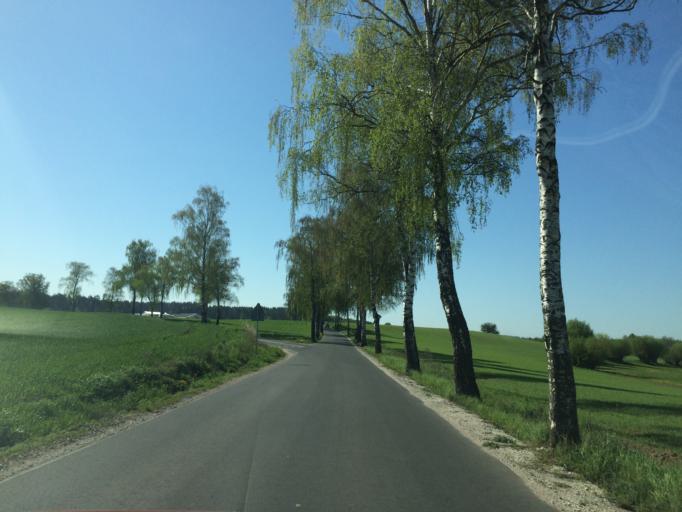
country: PL
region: Warmian-Masurian Voivodeship
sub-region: Powiat nowomiejski
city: Nowe Miasto Lubawskie
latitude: 53.5014
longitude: 19.5763
